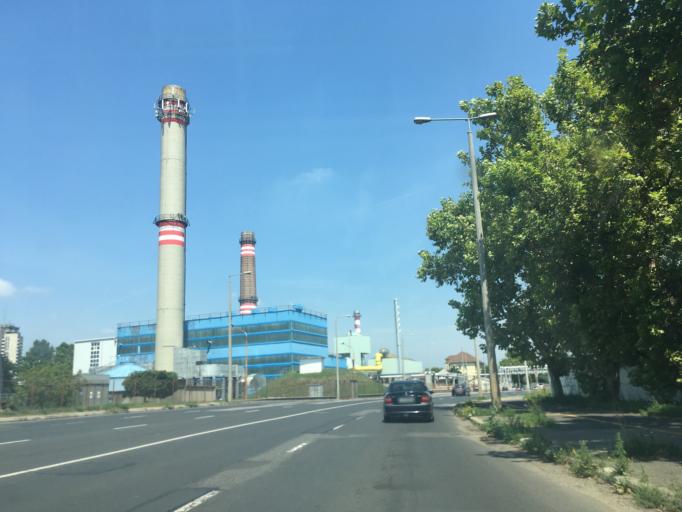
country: HU
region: Hajdu-Bihar
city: Debrecen
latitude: 47.5160
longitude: 21.6294
